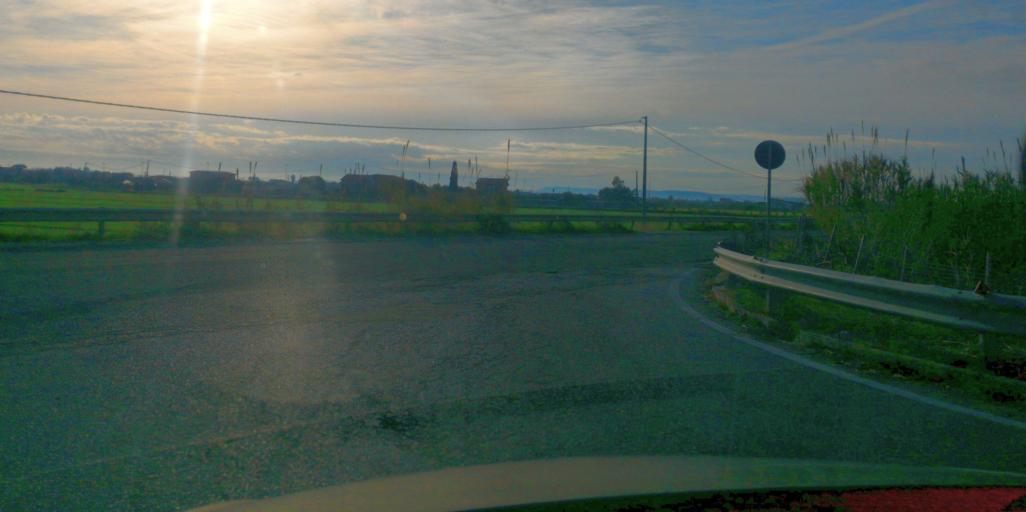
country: IT
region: Calabria
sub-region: Provincia di Crotone
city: Tronca
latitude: 39.1655
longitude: 17.0994
